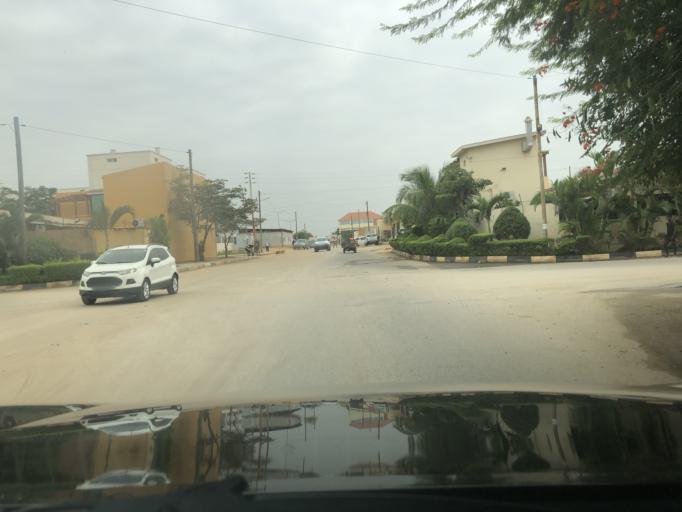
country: AO
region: Luanda
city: Luanda
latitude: -8.9427
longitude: 13.2517
